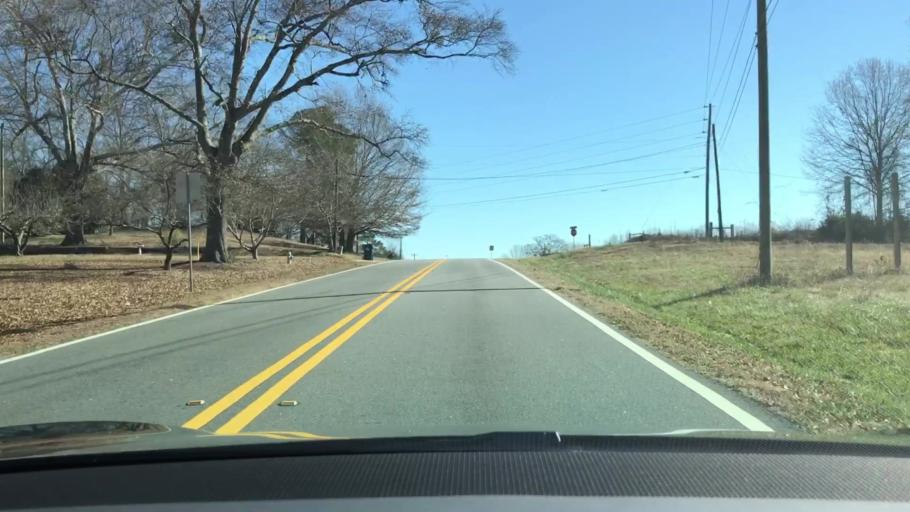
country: US
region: Georgia
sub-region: Walton County
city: Loganville
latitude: 33.9035
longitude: -83.8097
